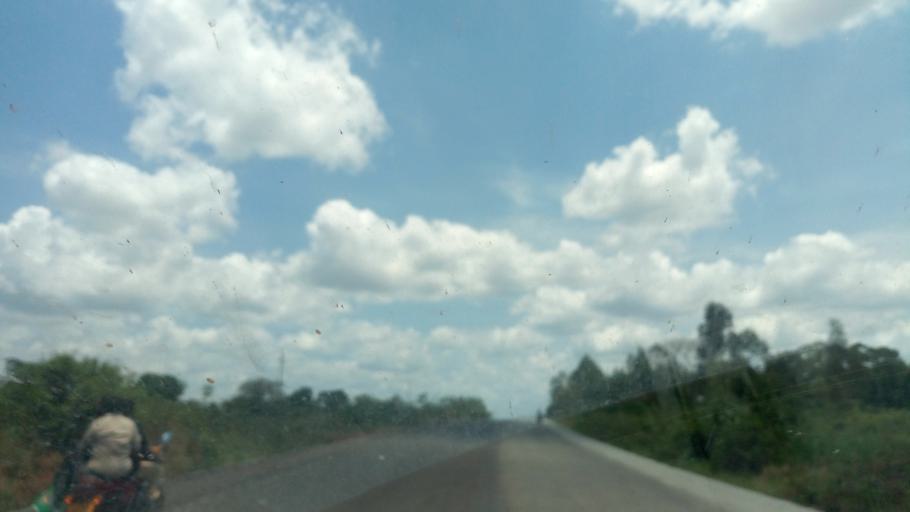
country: UG
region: Western Region
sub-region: Kiryandongo District
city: Kiryandongo
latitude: 1.7904
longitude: 31.9433
